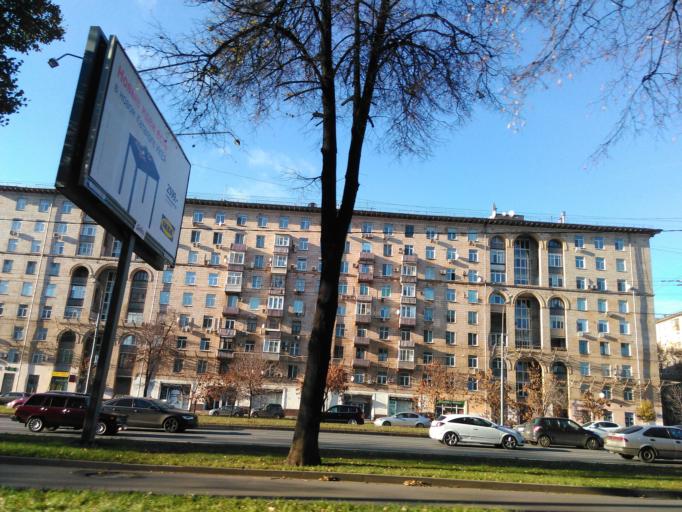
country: RU
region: Moskovskaya
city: Semenovskoye
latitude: 55.6857
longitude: 37.5426
